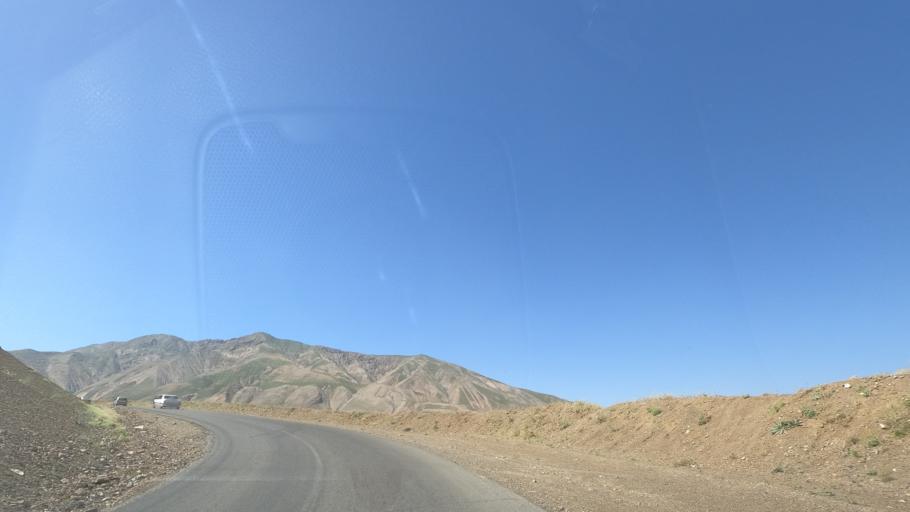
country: IR
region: Alborz
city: Karaj
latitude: 35.9365
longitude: 51.0813
